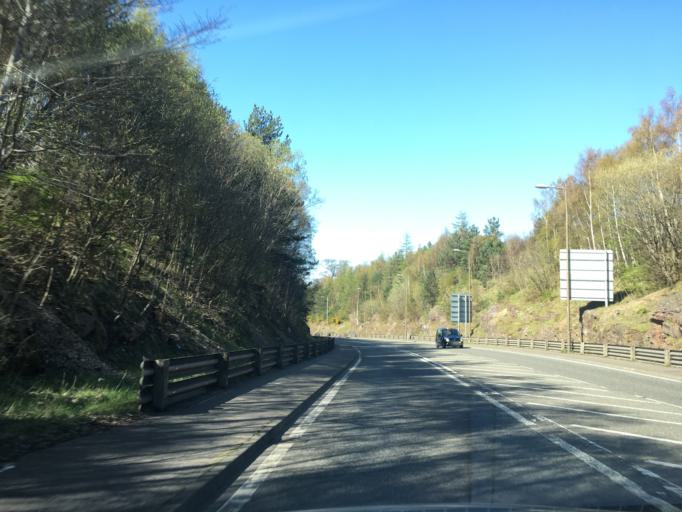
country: GB
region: Scotland
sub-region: Edinburgh
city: Colinton
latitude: 55.9007
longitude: -3.2310
